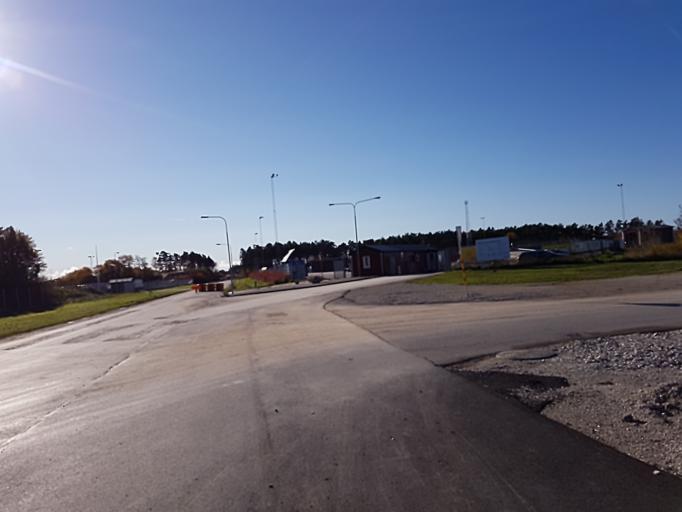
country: SE
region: Gotland
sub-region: Gotland
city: Visby
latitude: 57.6242
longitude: 18.3172
